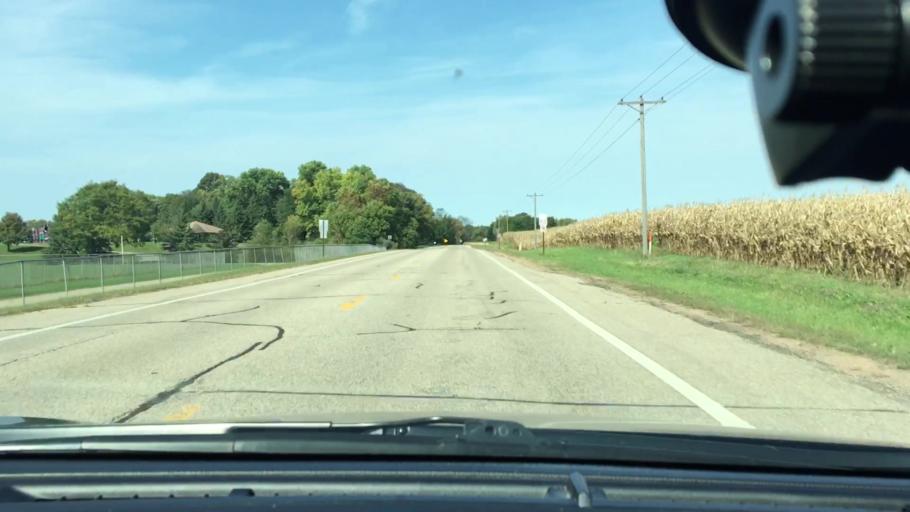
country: US
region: Minnesota
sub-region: Hennepin County
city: Corcoran
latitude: 45.0964
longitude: -93.5499
